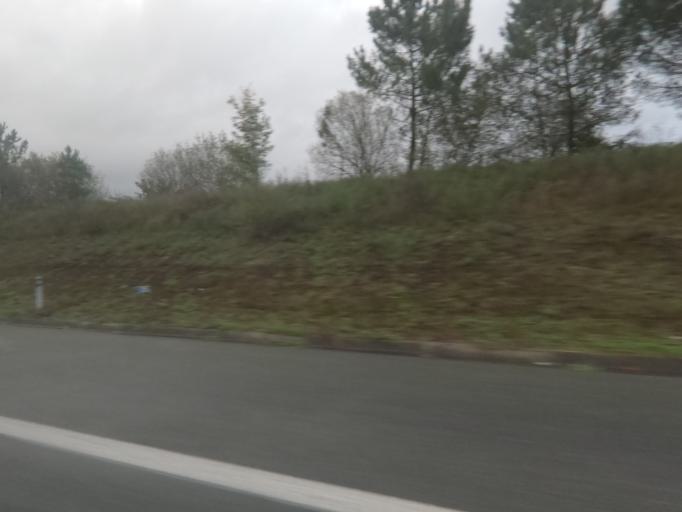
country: PT
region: Viana do Castelo
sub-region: Ponte de Lima
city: Ponte de Lima
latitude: 41.7906
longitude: -8.5766
